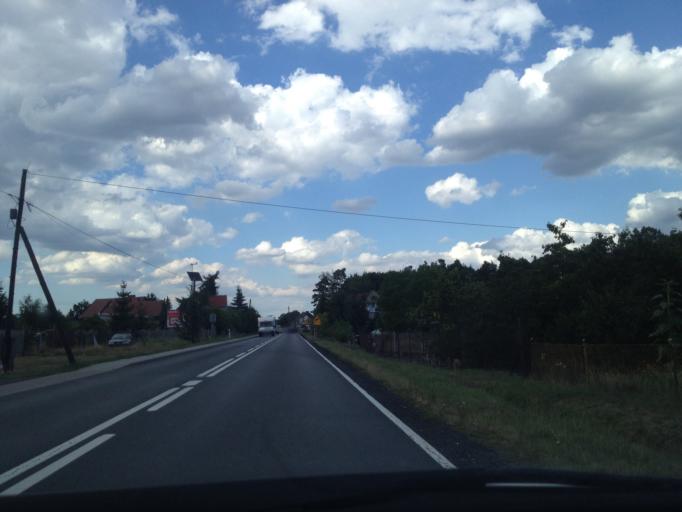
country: PL
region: Lubusz
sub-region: Powiat zarski
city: Zary
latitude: 51.6121
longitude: 15.1052
